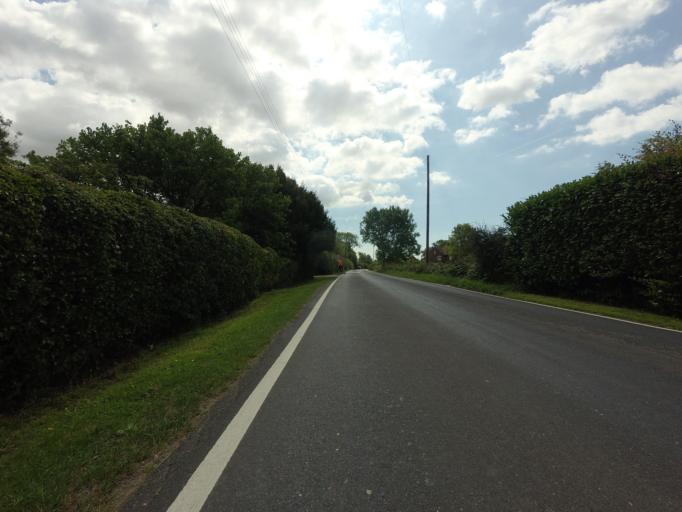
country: GB
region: England
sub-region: Kent
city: Stone
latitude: 51.0452
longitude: 0.7831
